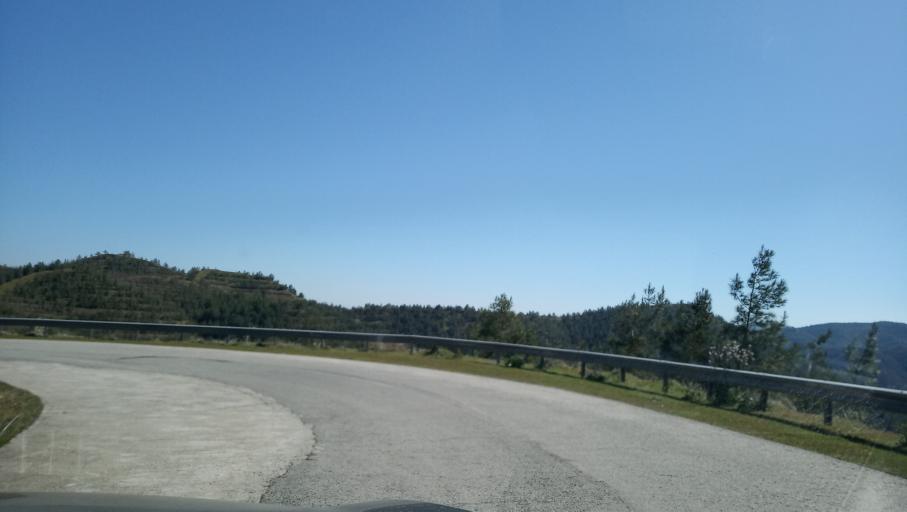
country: CY
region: Lefkosia
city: Lefka
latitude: 35.0816
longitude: 32.7793
